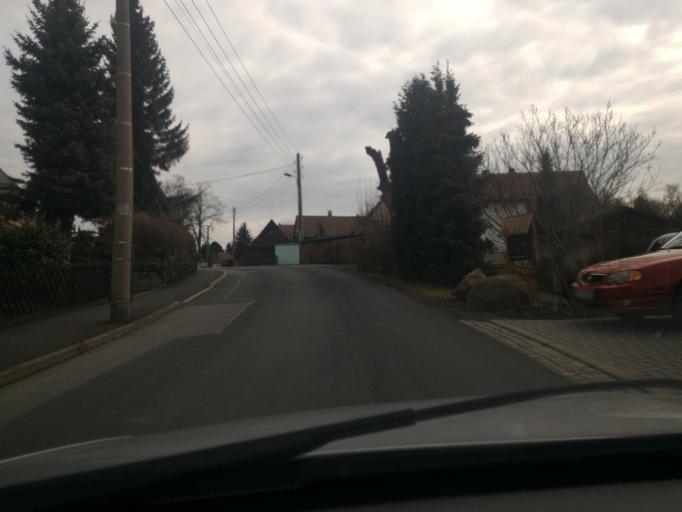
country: DE
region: Saxony
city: Olbersdorf
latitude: 50.8656
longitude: 14.7667
